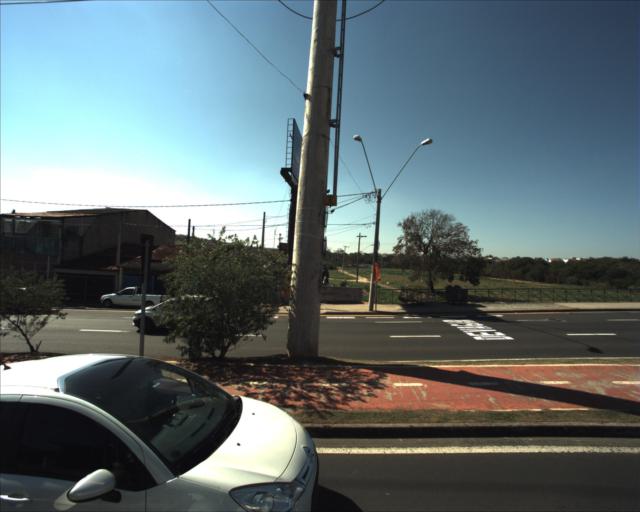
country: BR
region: Sao Paulo
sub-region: Sorocaba
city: Sorocaba
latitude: -23.4531
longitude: -47.4628
